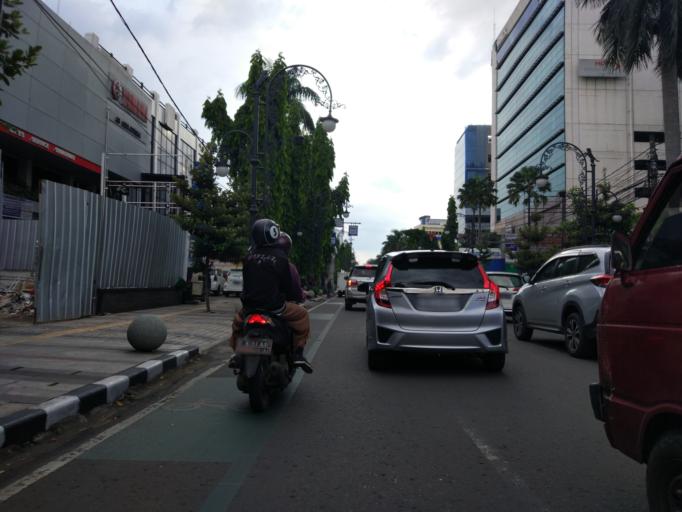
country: ID
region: West Java
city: Bandung
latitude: -6.9224
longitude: 107.6167
